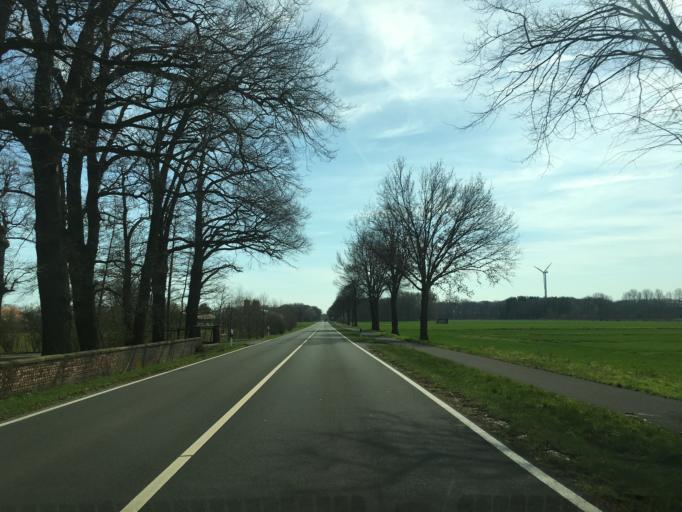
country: DE
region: North Rhine-Westphalia
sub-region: Regierungsbezirk Munster
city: Greven
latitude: 52.0637
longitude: 7.6132
